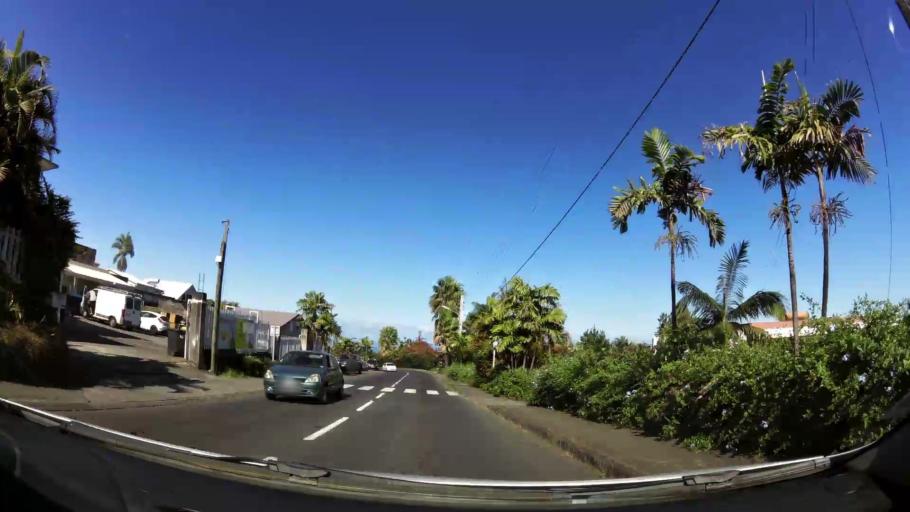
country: RE
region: Reunion
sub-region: Reunion
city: Le Tampon
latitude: -21.2688
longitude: 55.5235
